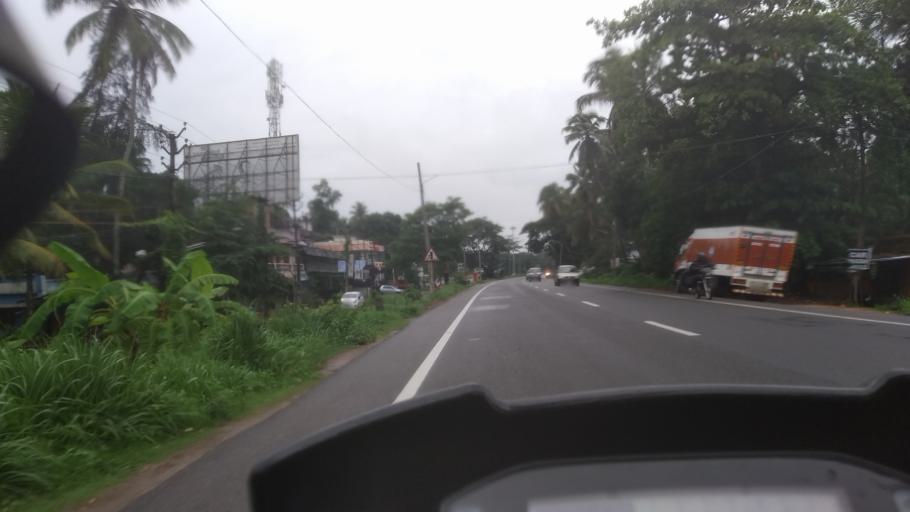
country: IN
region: Kerala
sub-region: Alappuzha
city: Kayankulam
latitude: 9.1806
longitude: 76.4920
